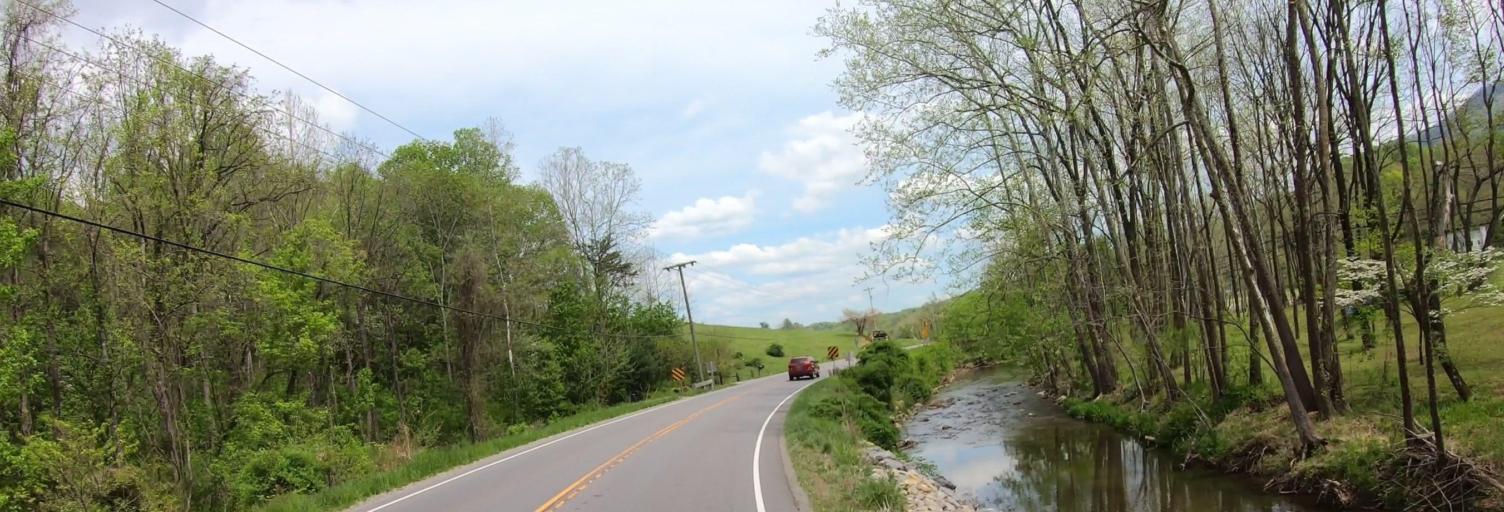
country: US
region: Virginia
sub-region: Roanoke County
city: Cave Spring
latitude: 37.1997
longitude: -80.0542
